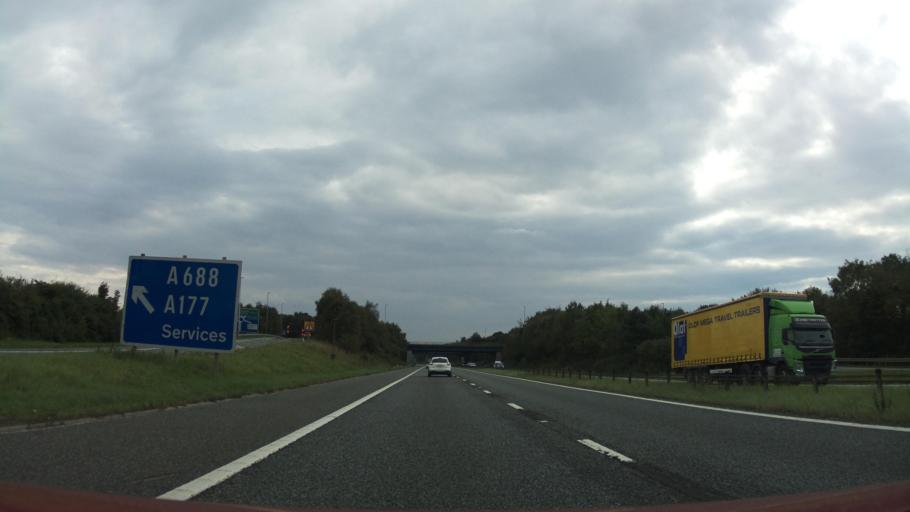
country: GB
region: England
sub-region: County Durham
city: Coxhoe
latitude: 54.7332
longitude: -1.5179
